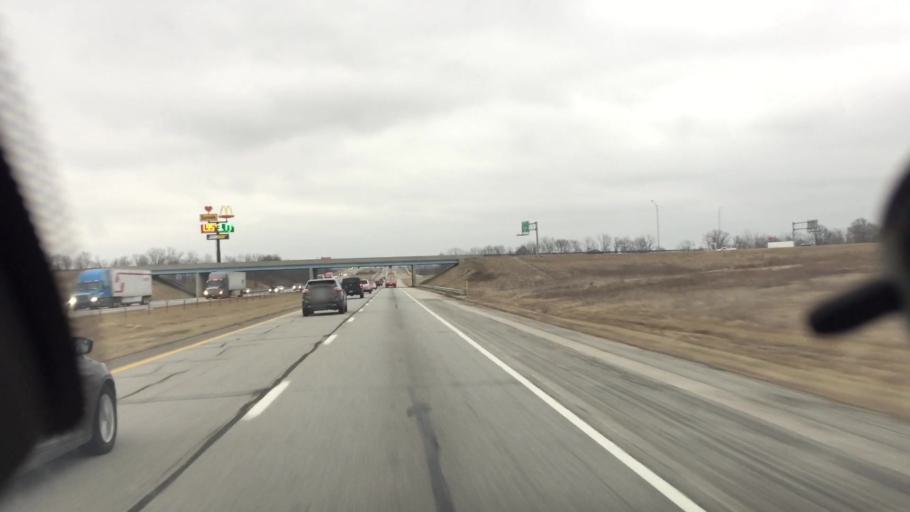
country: US
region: Indiana
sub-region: Henry County
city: Knightstown
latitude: 39.8394
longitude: -85.5569
